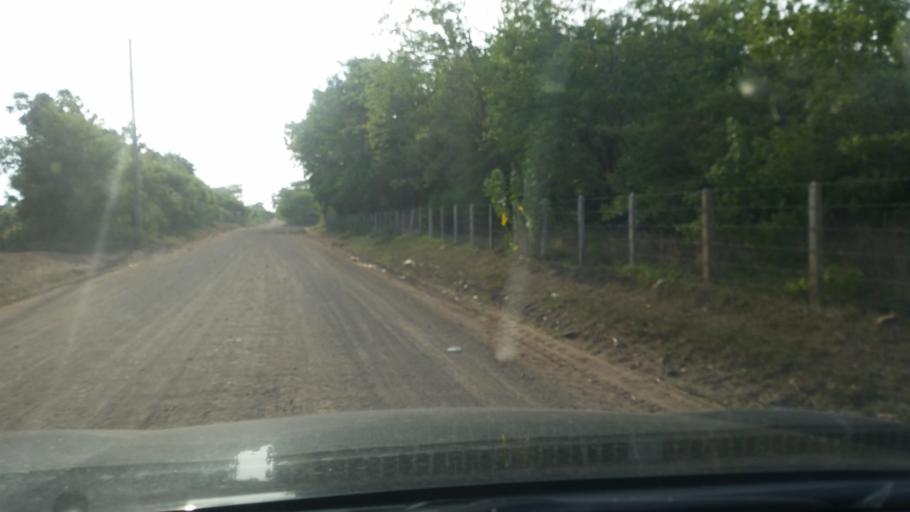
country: NI
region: Managua
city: Masachapa
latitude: 11.7687
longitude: -86.4892
